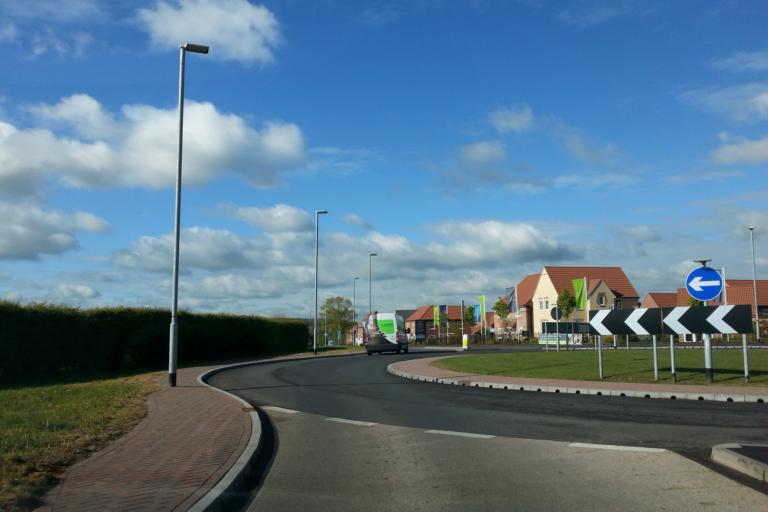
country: GB
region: England
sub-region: Nottinghamshire
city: Cotgrave
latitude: 52.9189
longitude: -1.0272
